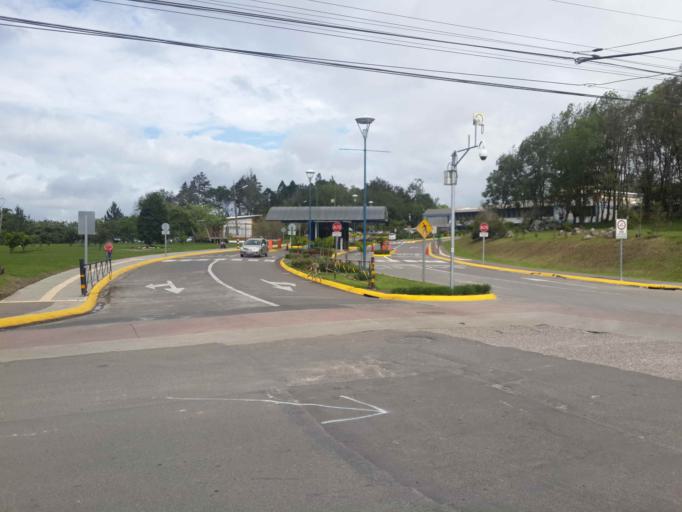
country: CR
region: Cartago
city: Cartago
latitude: 9.8582
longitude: -83.9134
